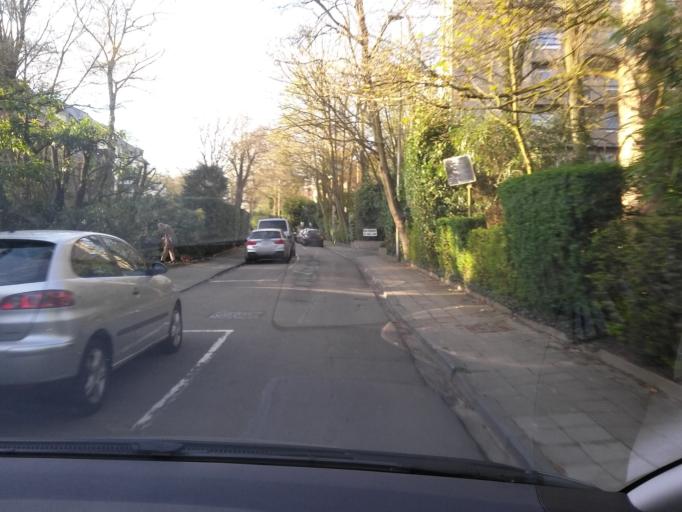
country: BE
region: Flanders
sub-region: Provincie Vlaams-Brabant
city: Hoeilaart
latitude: 50.7981
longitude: 4.4066
